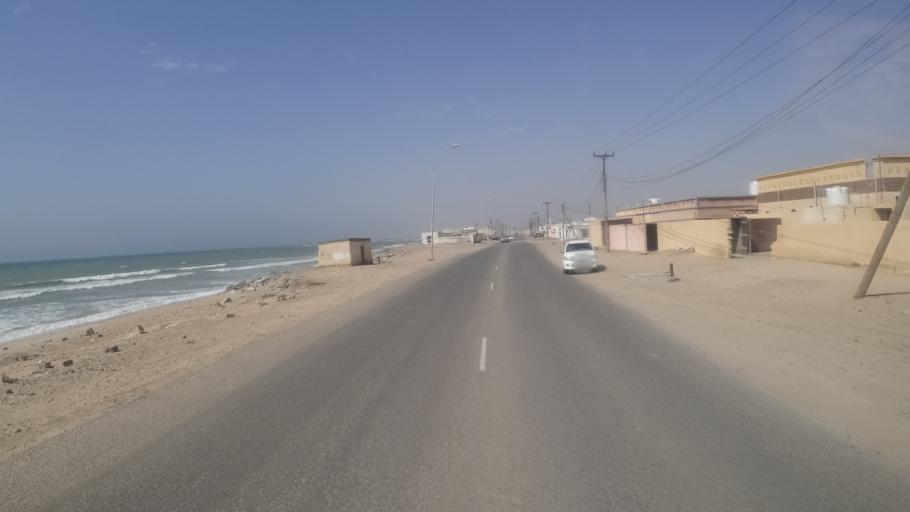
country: OM
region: Ash Sharqiyah
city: Sur
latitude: 22.1202
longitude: 59.7179
